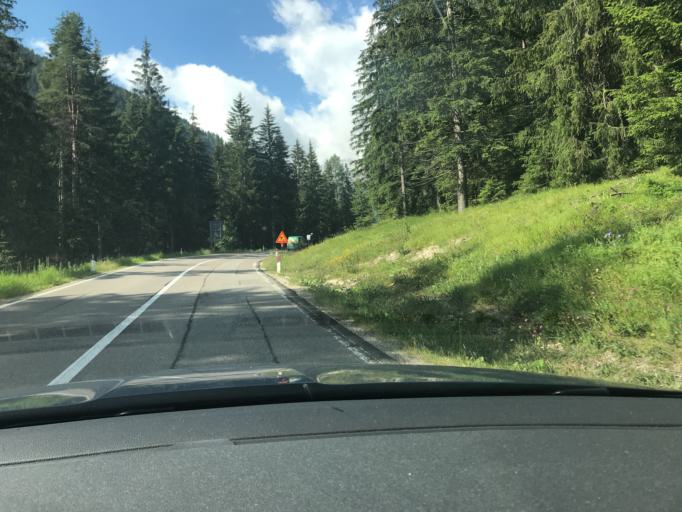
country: IT
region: Trentino-Alto Adige
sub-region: Bolzano
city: Corvara in Badia
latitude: 46.5651
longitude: 11.8869
